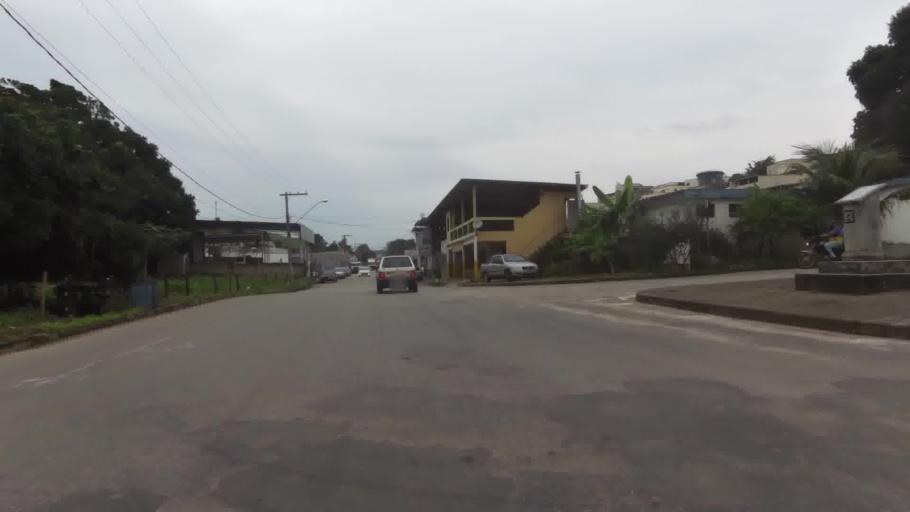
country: BR
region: Espirito Santo
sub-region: Iconha
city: Iconha
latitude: -20.7898
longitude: -40.8103
